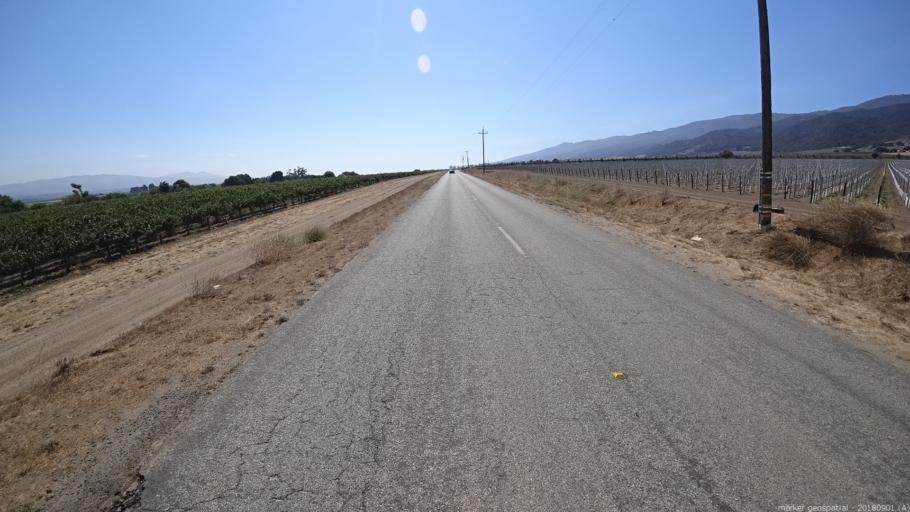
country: US
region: California
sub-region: Monterey County
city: Gonzales
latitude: 36.4912
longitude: -121.4937
